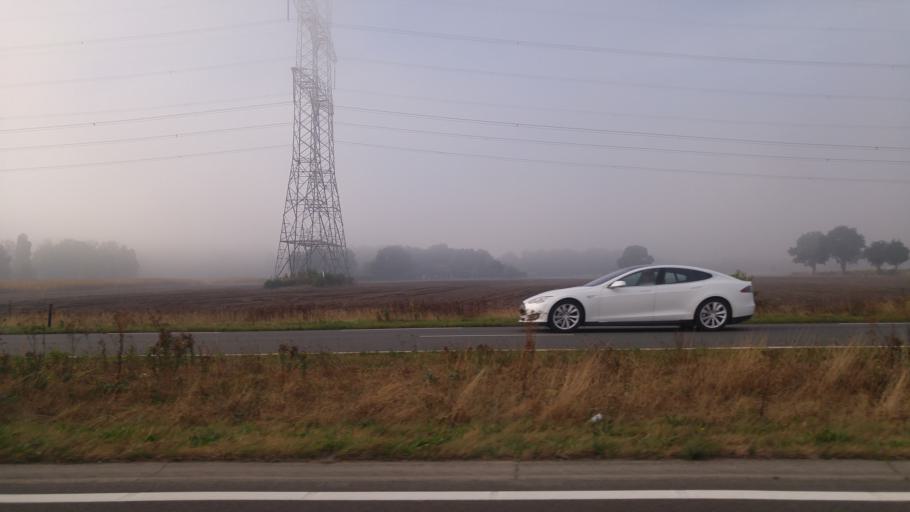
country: NL
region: North Brabant
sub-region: Gemeente Loon op Zand
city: Loon op Zand
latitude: 51.5978
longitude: 5.0947
